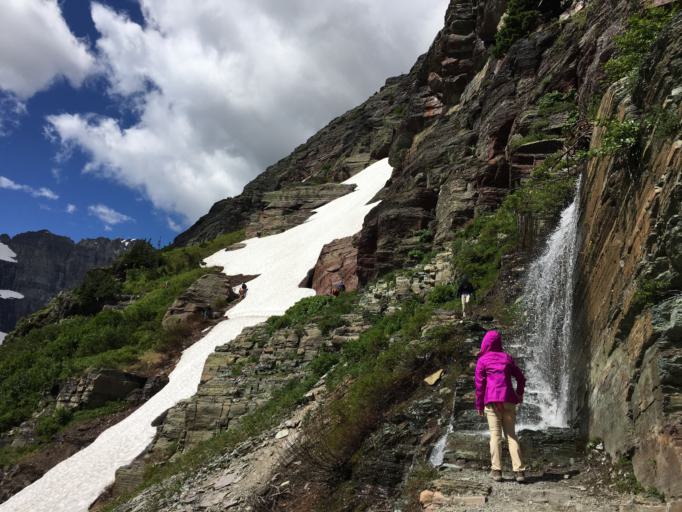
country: CA
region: Alberta
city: Cardston
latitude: 48.7739
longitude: -113.7129
